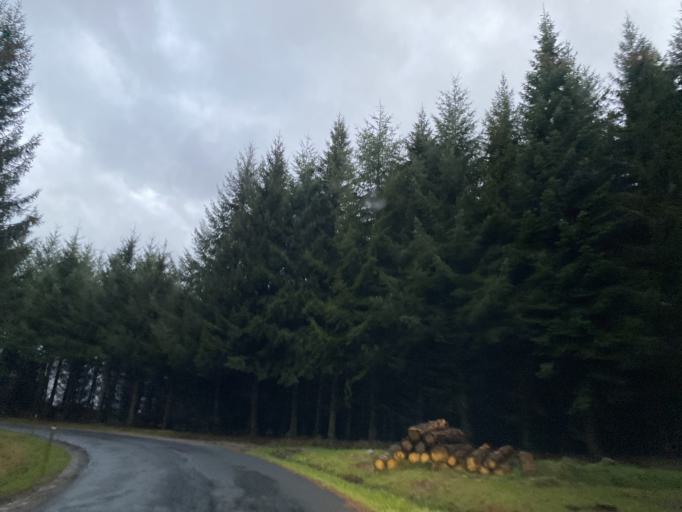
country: FR
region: Auvergne
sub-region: Departement du Puy-de-Dome
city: Cunlhat
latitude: 45.5506
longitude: 3.5721
